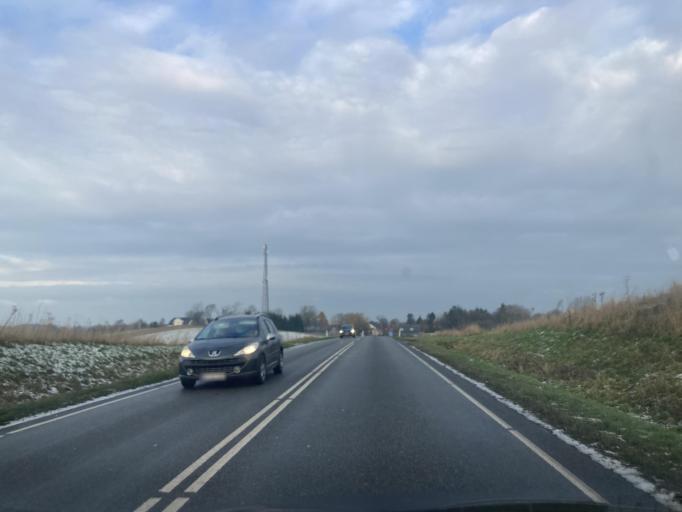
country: DK
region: Zealand
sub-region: Holbaek Kommune
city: Jyderup
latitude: 55.7057
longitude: 11.3856
